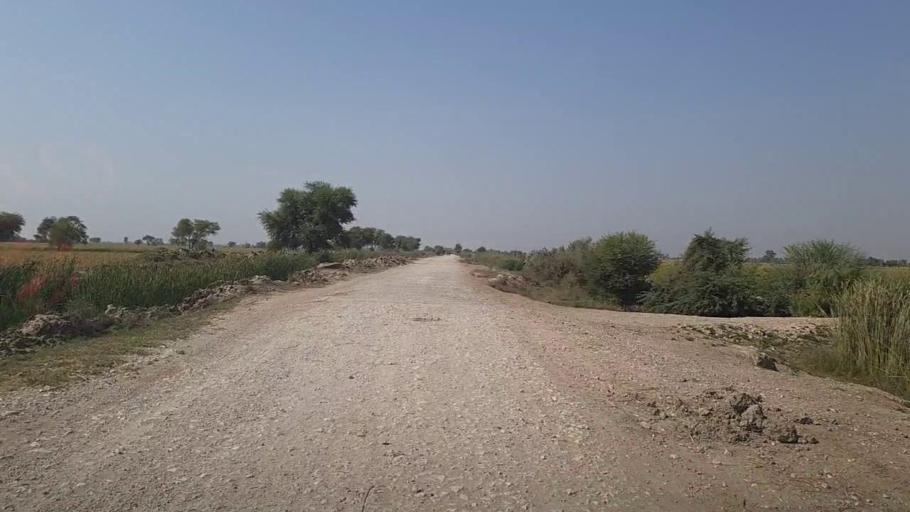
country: PK
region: Sindh
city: Kandhkot
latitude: 28.3975
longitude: 69.2697
